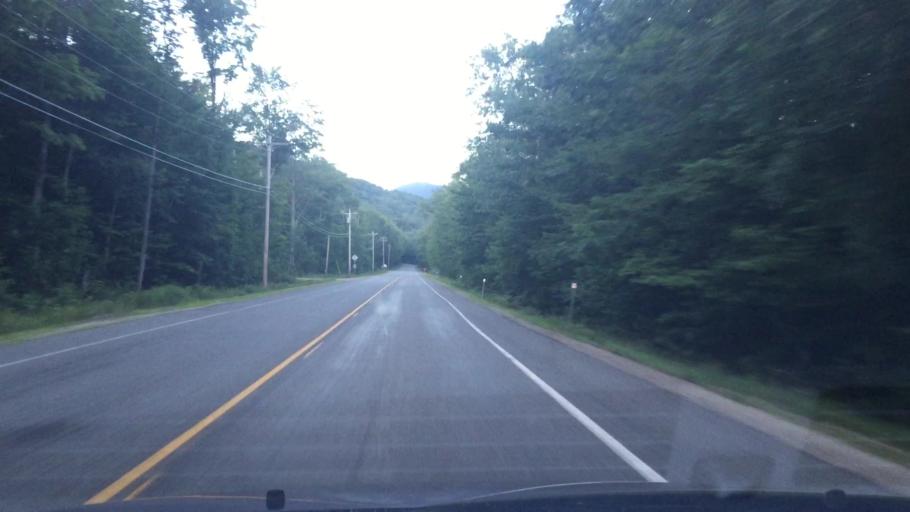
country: US
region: New Hampshire
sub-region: Grafton County
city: Woodstock
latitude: 44.0627
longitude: -71.6124
